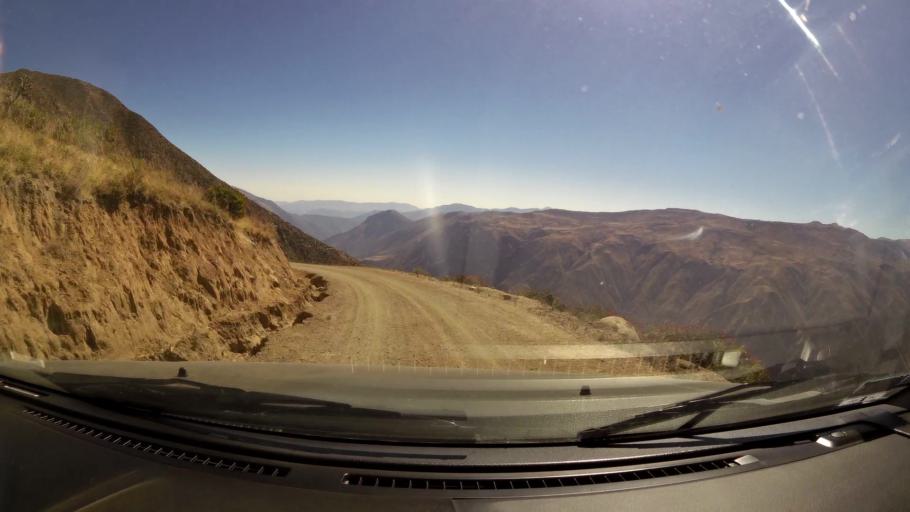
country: PE
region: Huancavelica
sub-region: Huaytara
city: Quito-Arma
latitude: -13.6191
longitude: -75.3527
